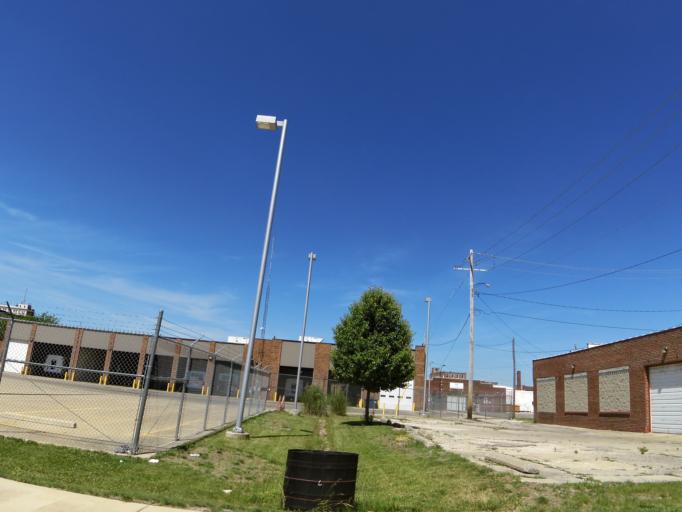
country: US
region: Illinois
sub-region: Vermilion County
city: Danville
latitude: 40.1271
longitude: -87.6261
